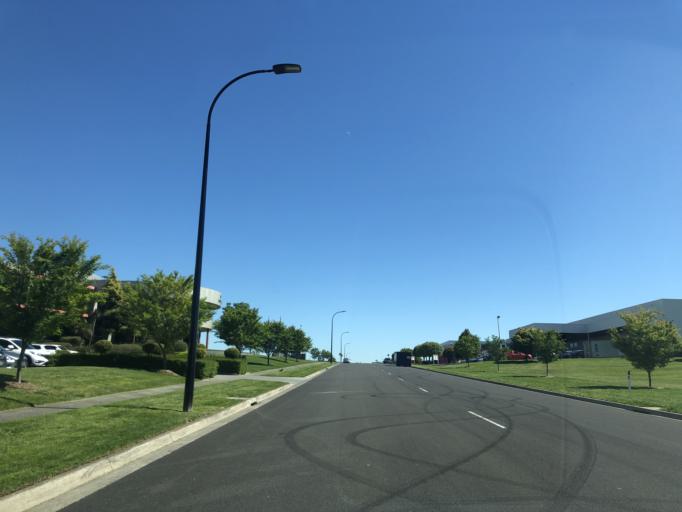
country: AU
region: Victoria
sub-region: Knox
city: Scoresby
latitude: -37.9053
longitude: 145.2253
